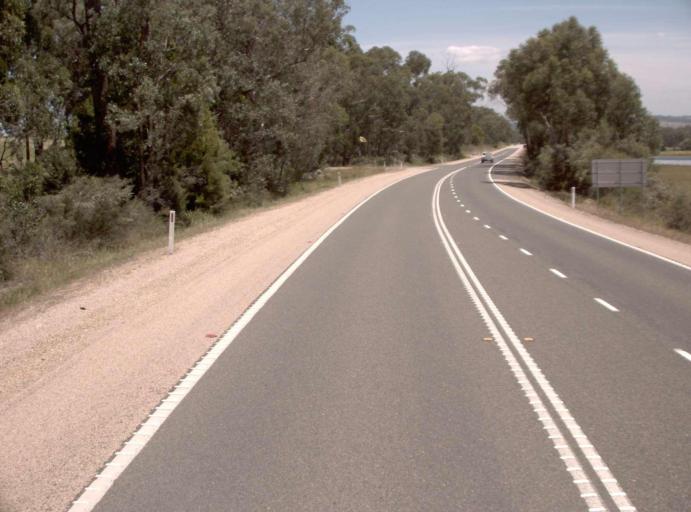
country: AU
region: Victoria
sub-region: East Gippsland
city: Bairnsdale
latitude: -37.7451
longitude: 147.7608
